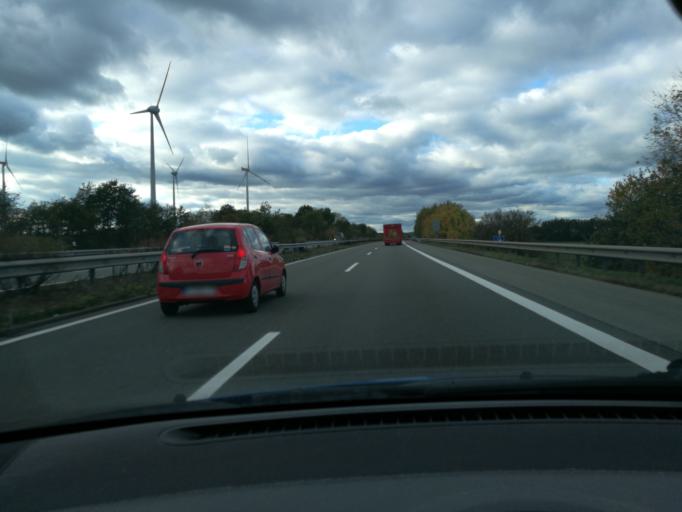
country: DE
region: Lower Saxony
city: Winsen
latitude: 53.3421
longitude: 10.1816
